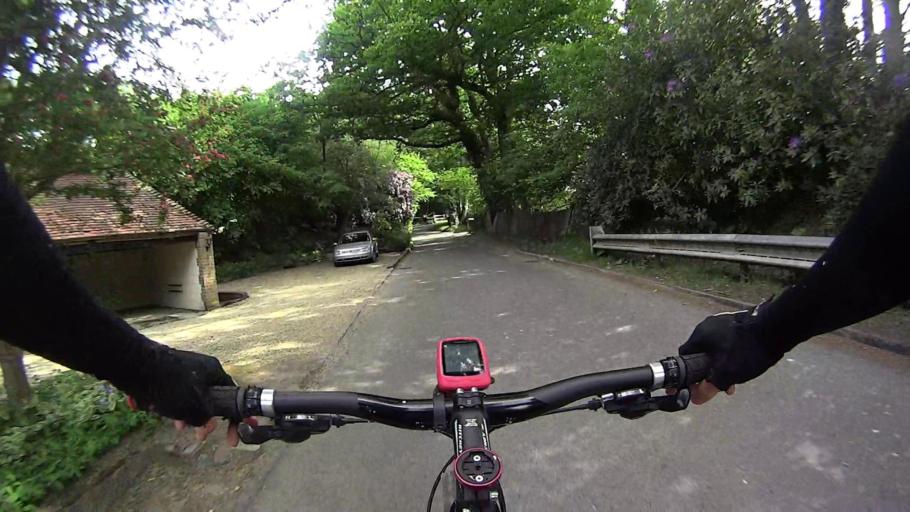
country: GB
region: England
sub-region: West Sussex
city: Horsham
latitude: 51.0475
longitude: -0.2621
